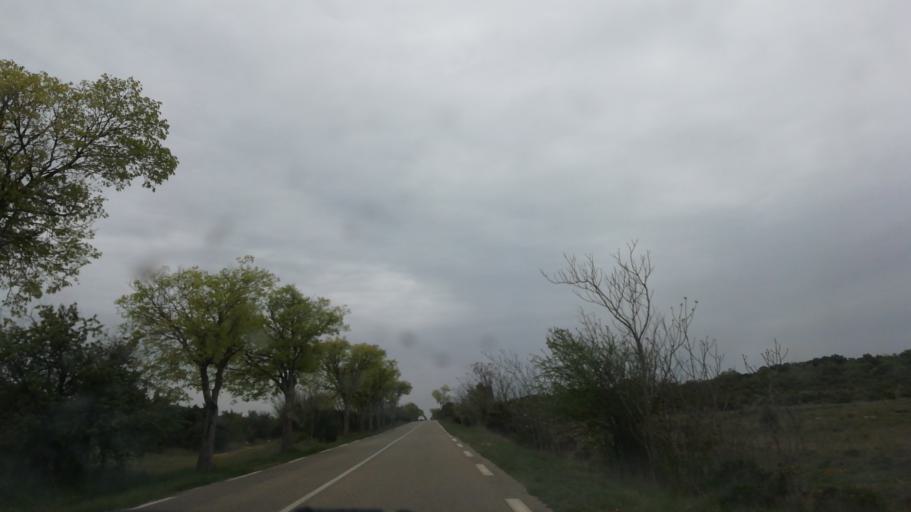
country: FR
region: Languedoc-Roussillon
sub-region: Departement de l'Herault
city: Saint-Martin-de-Londres
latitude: 43.7689
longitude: 3.7253
